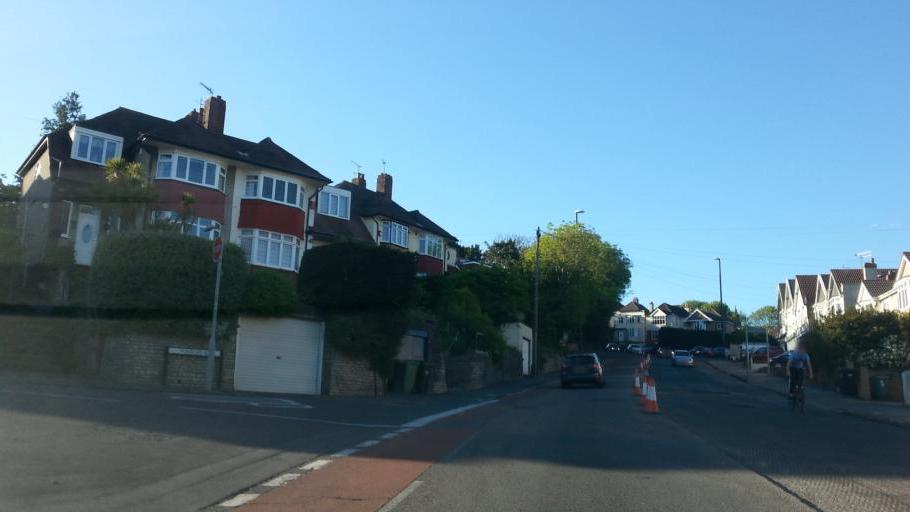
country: GB
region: England
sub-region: Bath and North East Somerset
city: Whitchurch
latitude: 51.4285
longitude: -2.5640
